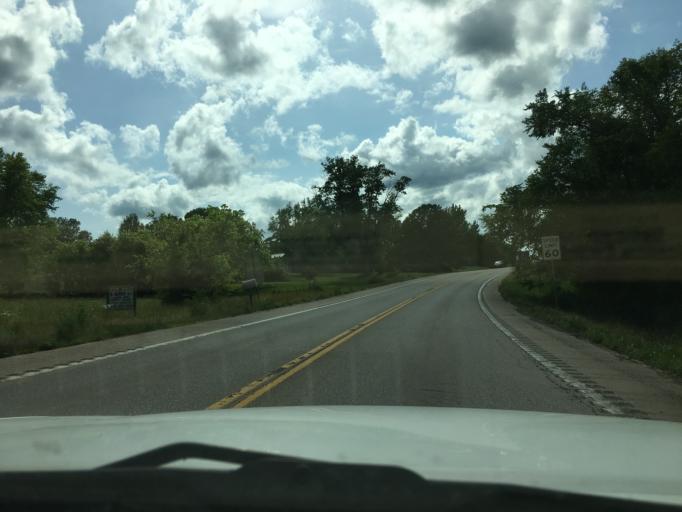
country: US
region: Missouri
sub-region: Franklin County
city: Gerald
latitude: 38.3947
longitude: -91.3430
